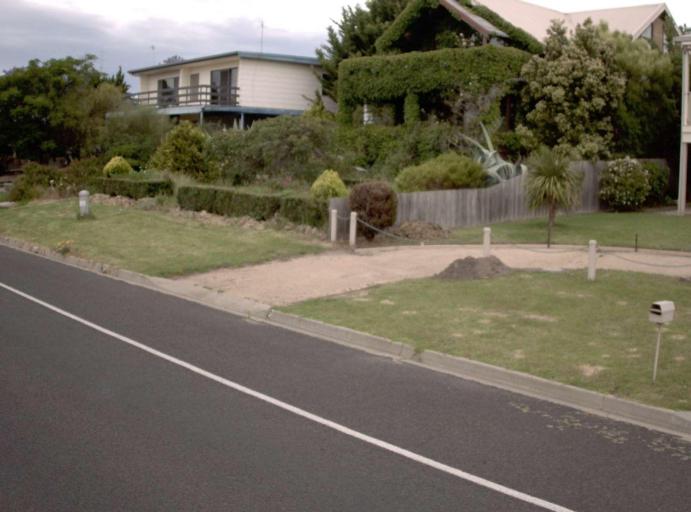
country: AU
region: Victoria
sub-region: East Gippsland
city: Bairnsdale
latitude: -37.9021
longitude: 147.6818
